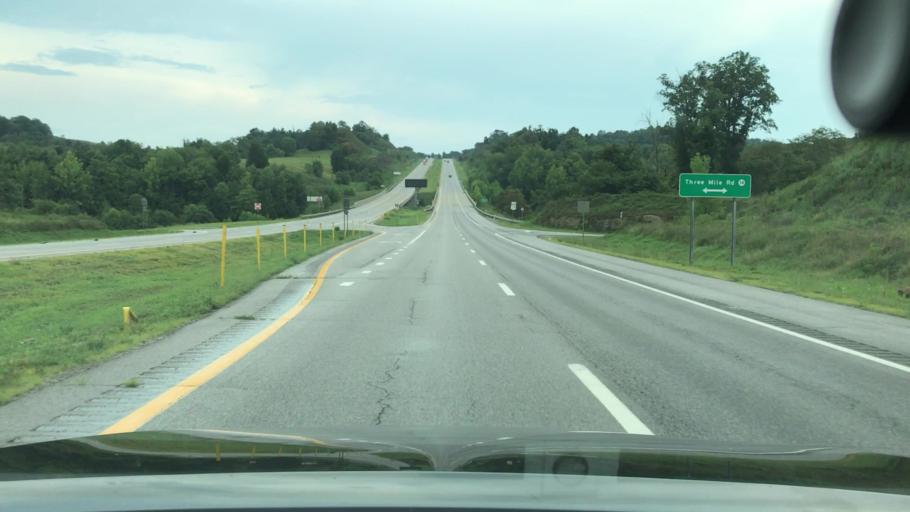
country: US
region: West Virginia
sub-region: Mason County
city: Point Pleasant
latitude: 38.8037
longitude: -82.1022
